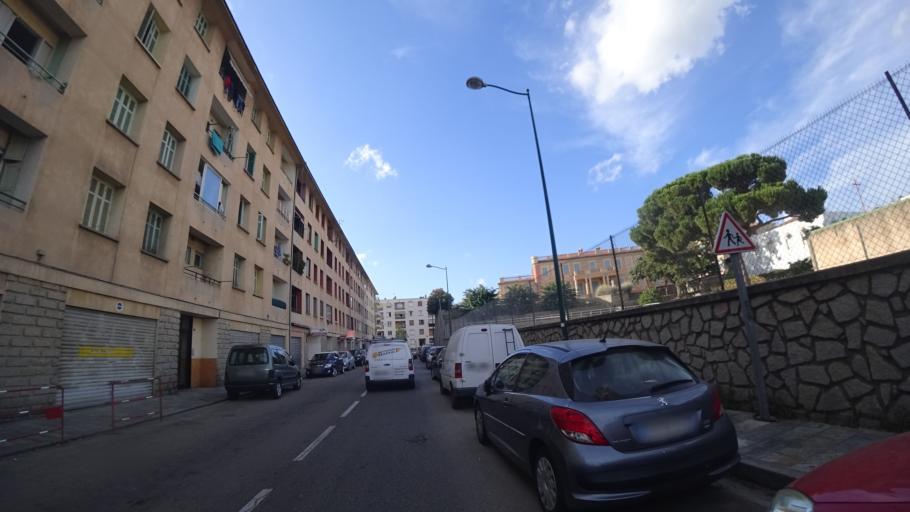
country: FR
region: Corsica
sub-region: Departement de la Corse-du-Sud
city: Ajaccio
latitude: 41.9339
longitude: 8.7439
